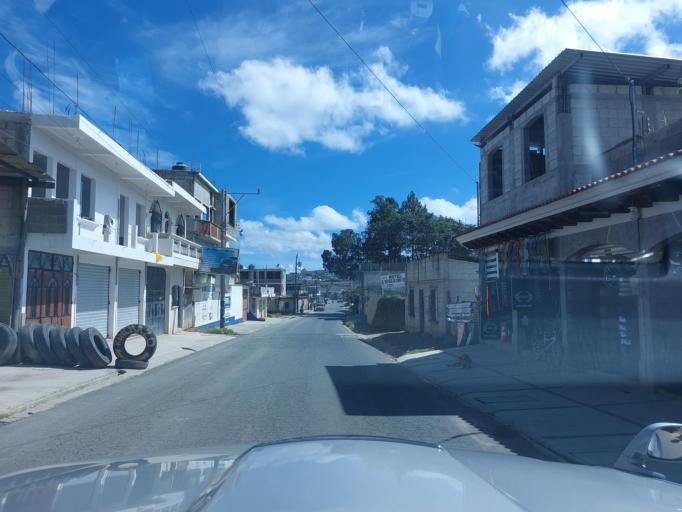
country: GT
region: Chimaltenango
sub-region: Municipio de San Juan Comalapa
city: Comalapa
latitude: 14.7278
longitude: -90.8874
